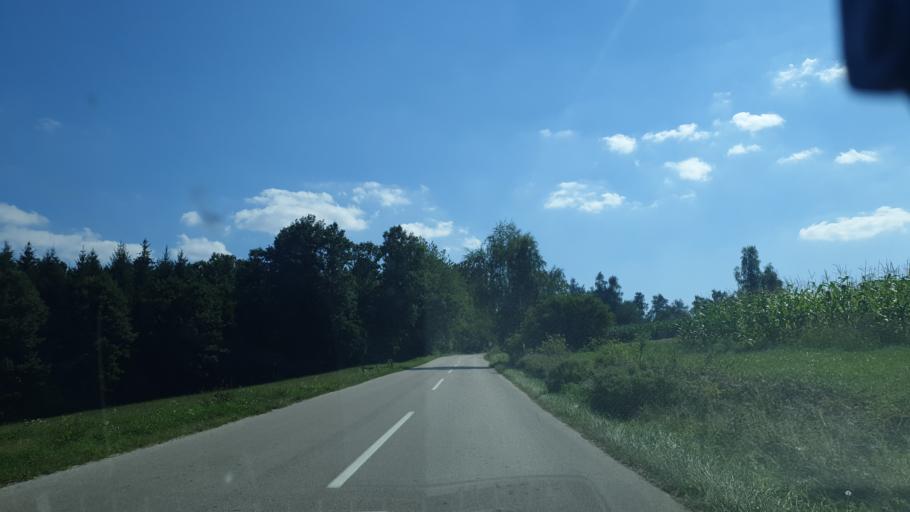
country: RS
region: Central Serbia
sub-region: Zlatiborski Okrug
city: Kosjeric
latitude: 44.0533
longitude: 20.0323
